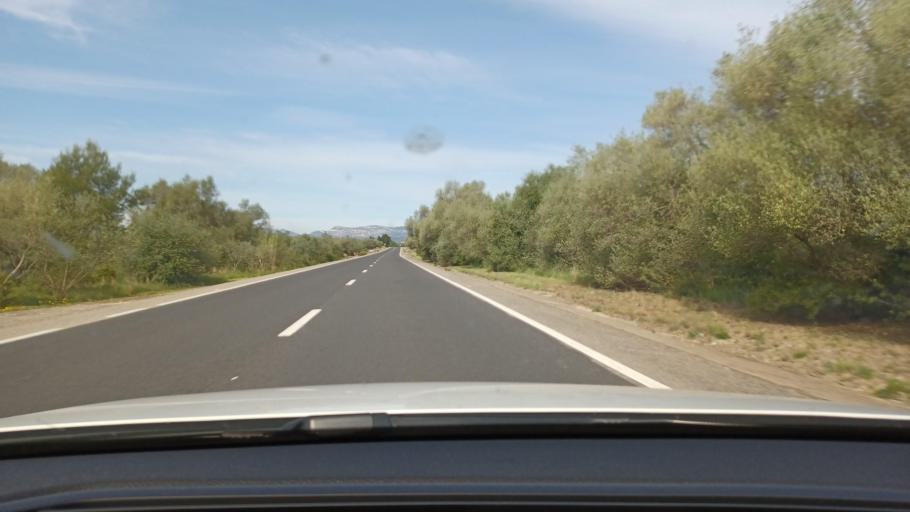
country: ES
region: Catalonia
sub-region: Provincia de Tarragona
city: Mas de Barberans
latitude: 40.6418
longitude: 0.3659
